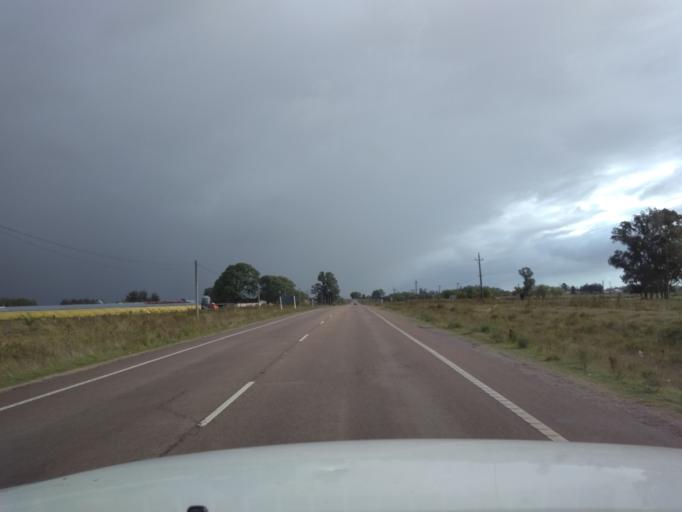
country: UY
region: Canelones
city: Tala
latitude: -34.3723
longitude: -55.7860
